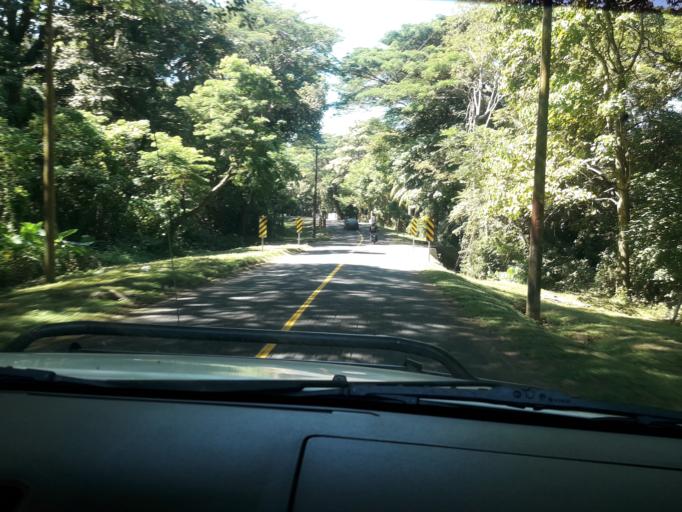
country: NI
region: Rivas
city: Cardenas
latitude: 11.2327
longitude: -85.5502
